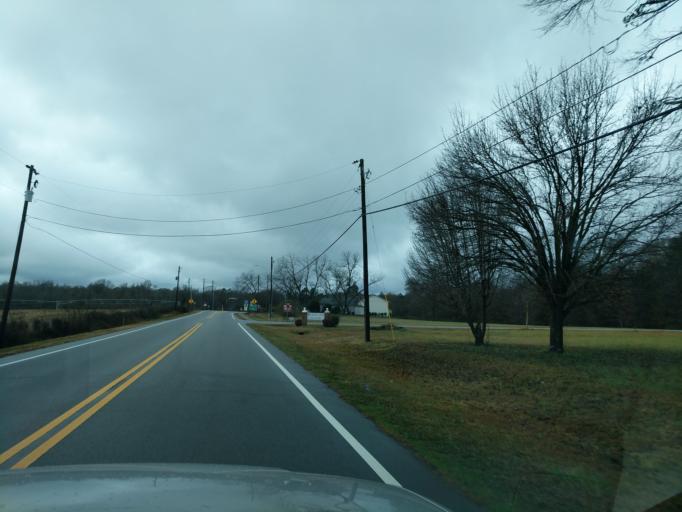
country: US
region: Georgia
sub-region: Hart County
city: Royston
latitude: 34.2882
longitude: -83.0925
